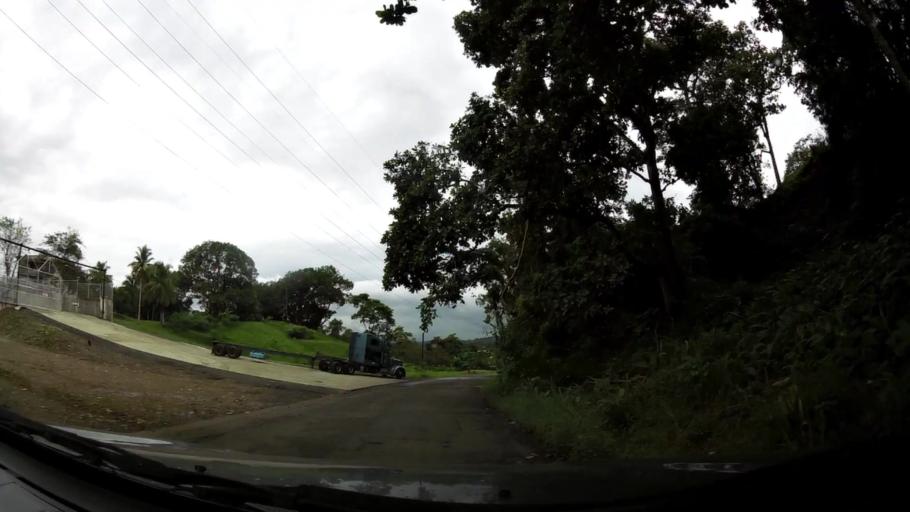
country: PA
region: Panama
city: Chilibre
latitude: 9.1373
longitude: -79.6144
